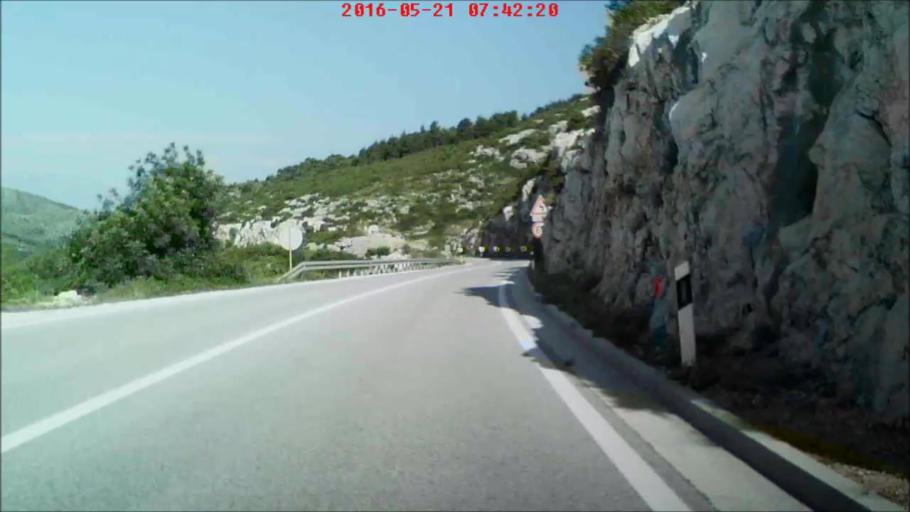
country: HR
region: Dubrovacko-Neretvanska
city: Podgora
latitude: 42.8100
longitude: 17.8050
